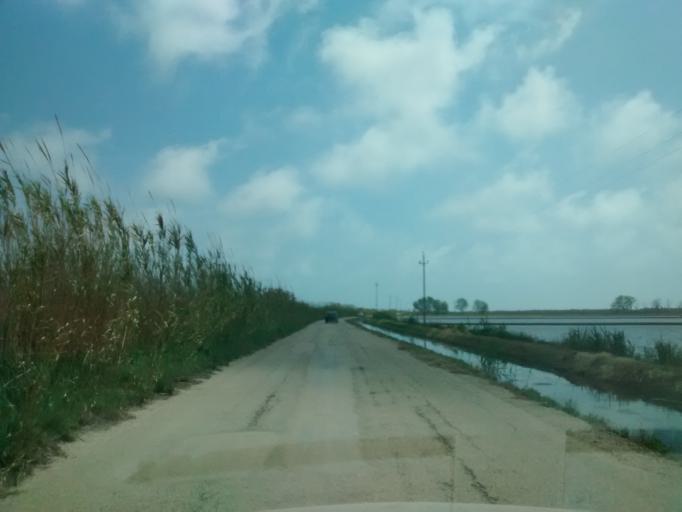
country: ES
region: Catalonia
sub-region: Provincia de Tarragona
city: Deltebre
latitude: 40.6976
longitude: 0.8341
